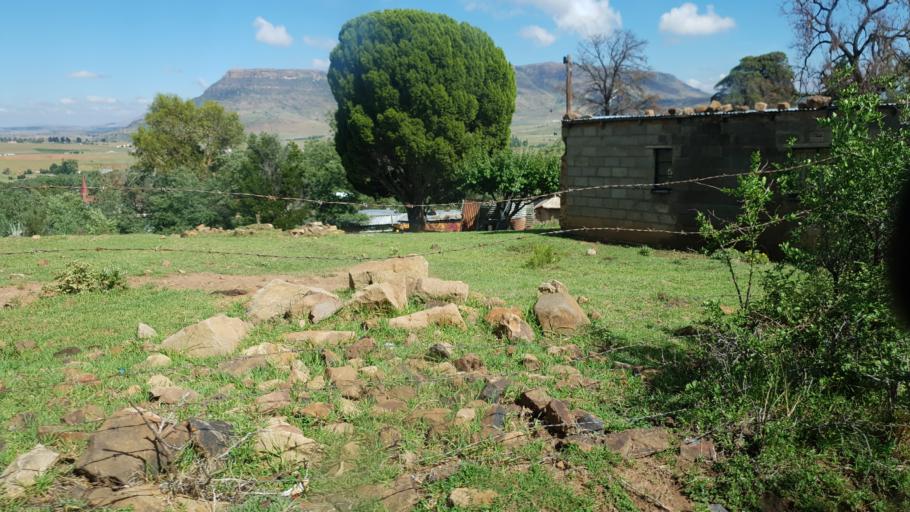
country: LS
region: Maseru
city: Nako
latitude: -29.6255
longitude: 27.5125
